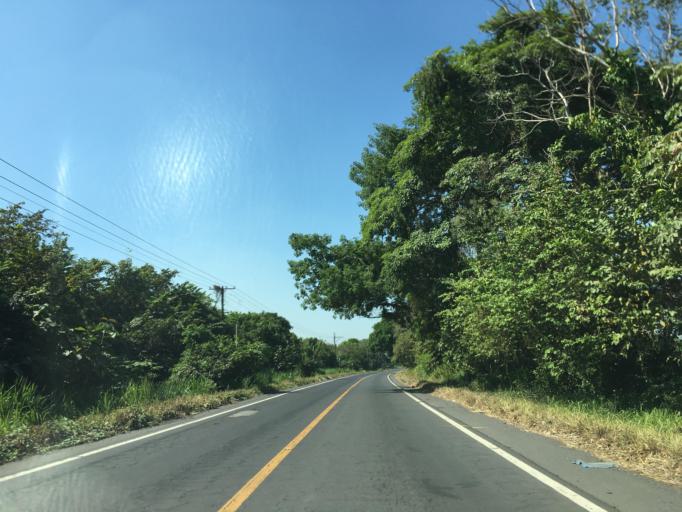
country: GT
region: Escuintla
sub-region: Municipio de Masagua
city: Masagua
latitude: 14.1759
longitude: -90.8702
